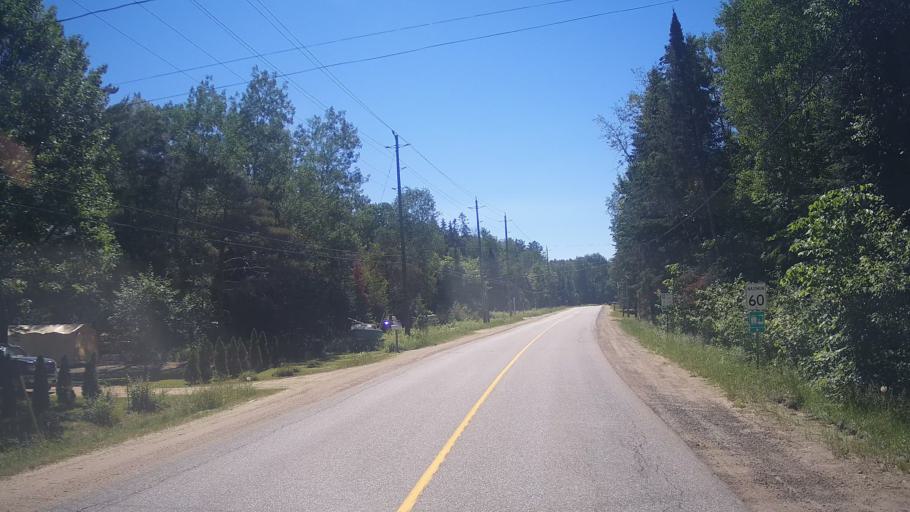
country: CA
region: Ontario
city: Huntsville
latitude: 45.3722
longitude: -79.2090
